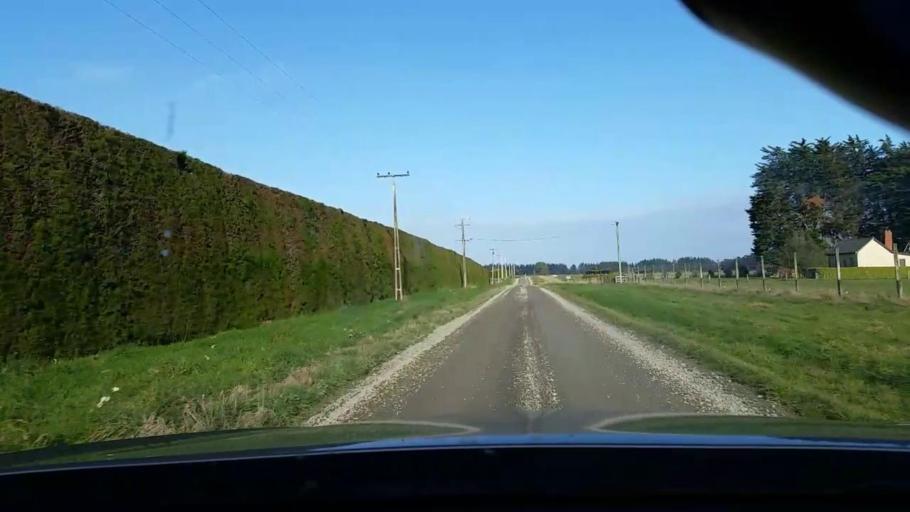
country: NZ
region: Southland
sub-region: Invercargill City
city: Invercargill
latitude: -46.2893
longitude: 168.2947
